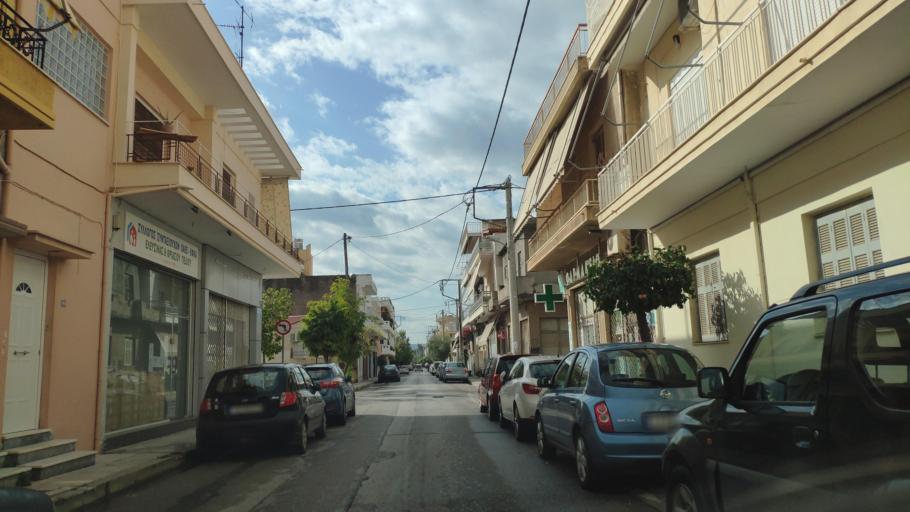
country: GR
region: Attica
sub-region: Nomarchia Dytikis Attikis
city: Elefsina
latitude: 38.0423
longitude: 23.5431
